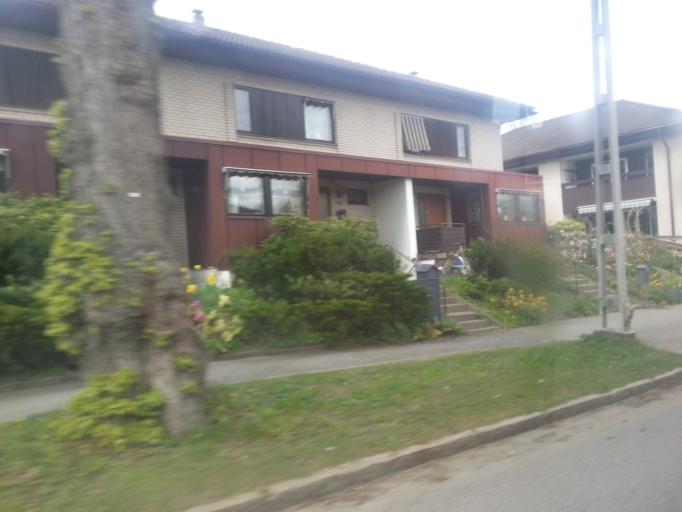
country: SE
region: OEstergoetland
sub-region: Norrkopings Kommun
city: Norrkoping
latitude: 58.5846
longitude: 16.1622
